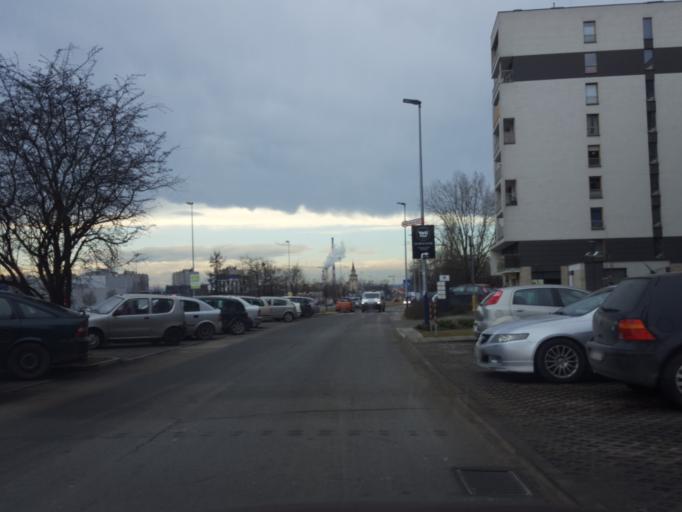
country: PL
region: Lesser Poland Voivodeship
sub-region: Krakow
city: Krakow
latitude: 50.0795
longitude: 20.0148
